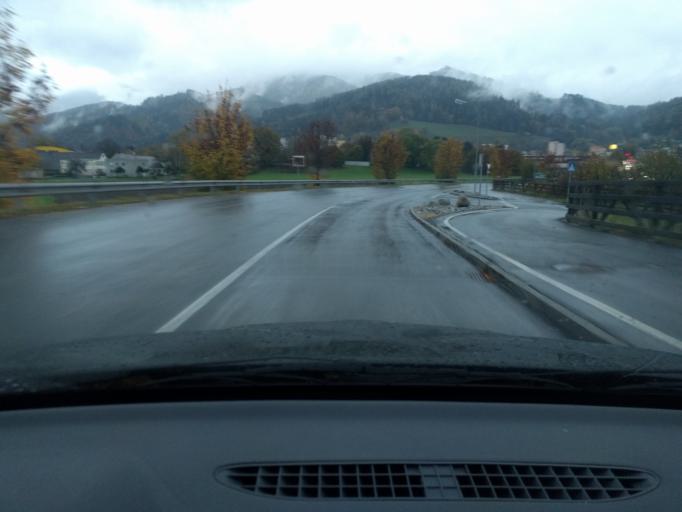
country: AT
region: Styria
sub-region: Politischer Bezirk Leoben
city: Leoben
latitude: 47.3861
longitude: 15.1049
